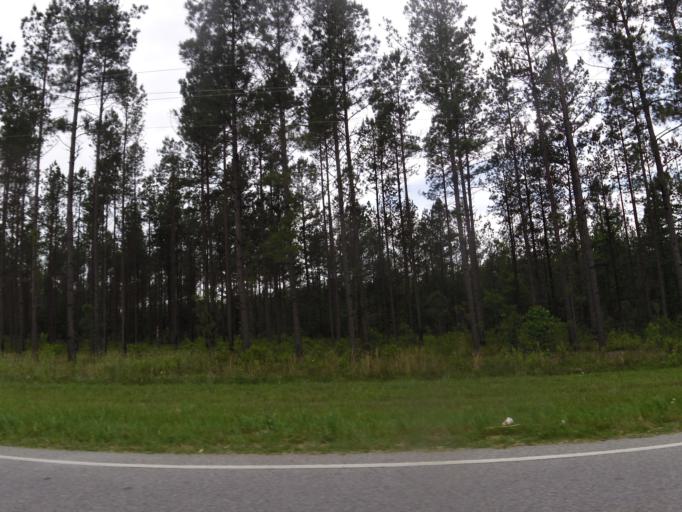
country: US
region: Georgia
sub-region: Emanuel County
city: Swainsboro
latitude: 32.4996
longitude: -82.2542
